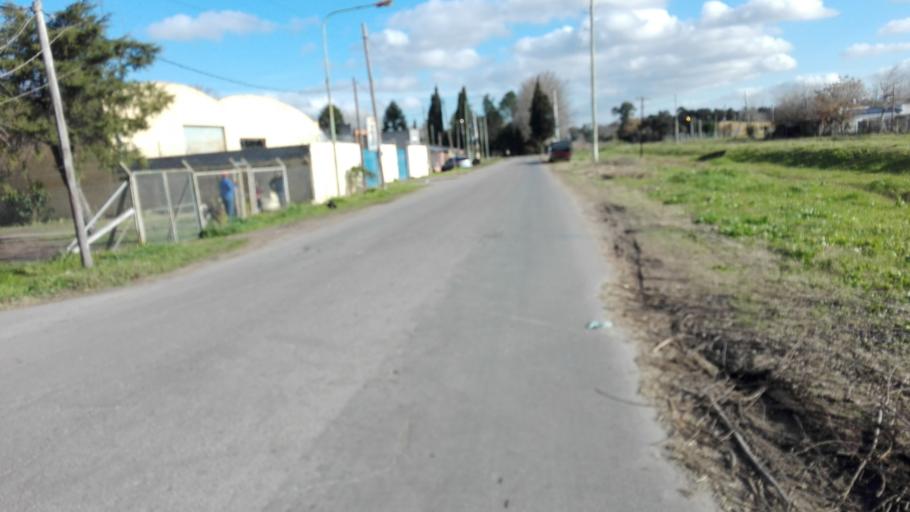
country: AR
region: Buenos Aires
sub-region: Partido de La Plata
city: La Plata
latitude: -34.9132
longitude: -58.0235
